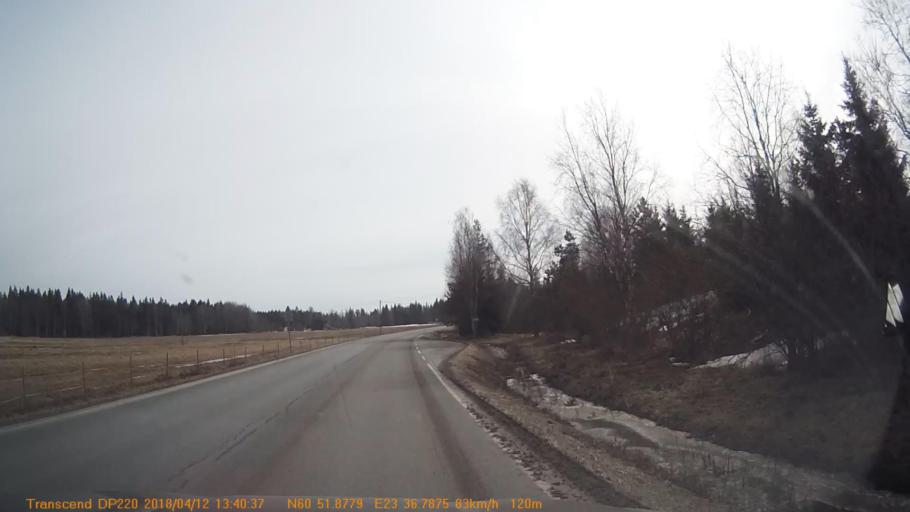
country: FI
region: Haeme
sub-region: Forssa
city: Forssa
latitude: 60.8640
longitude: 23.6136
